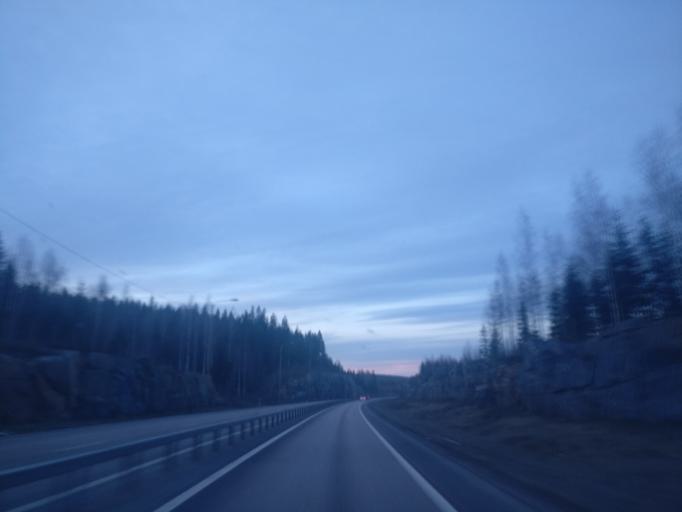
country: FI
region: Central Finland
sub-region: Jyvaeskylae
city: Saeynaetsalo
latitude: 62.2135
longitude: 25.8902
